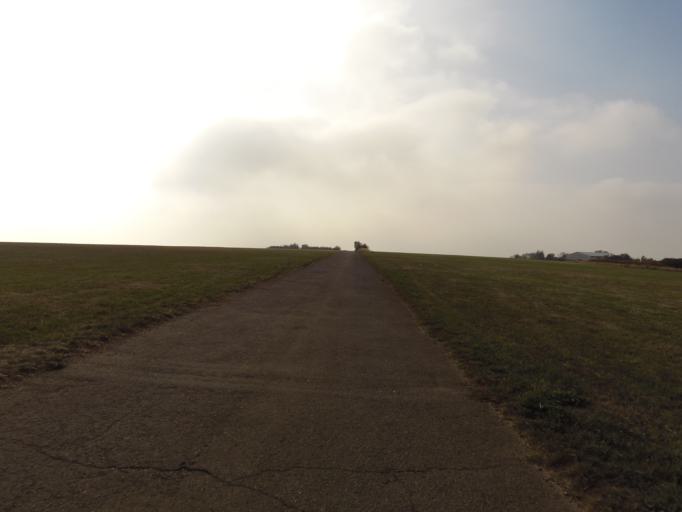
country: DE
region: Rheinland-Pfalz
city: Quirnheim
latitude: 49.5886
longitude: 8.1398
